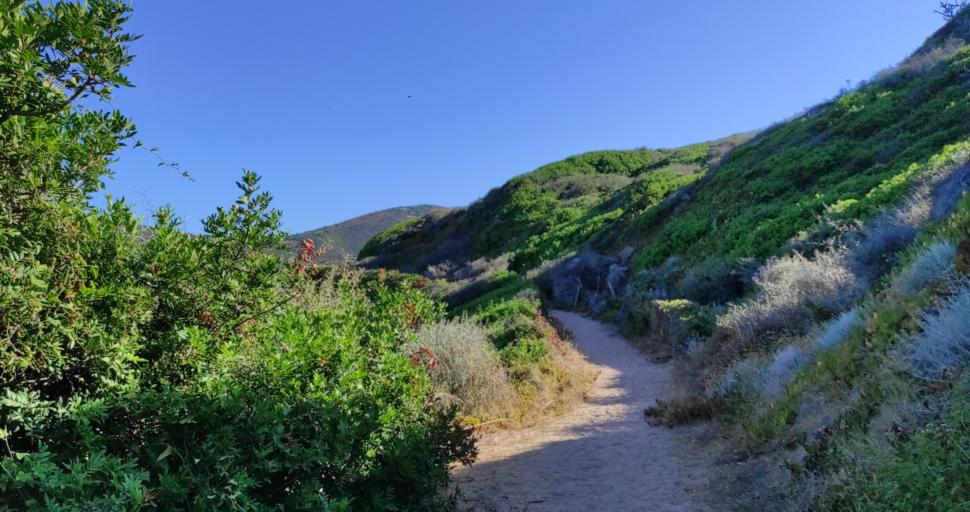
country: FR
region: Corsica
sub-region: Departement de la Corse-du-Sud
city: Alata
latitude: 41.9841
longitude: 8.6699
